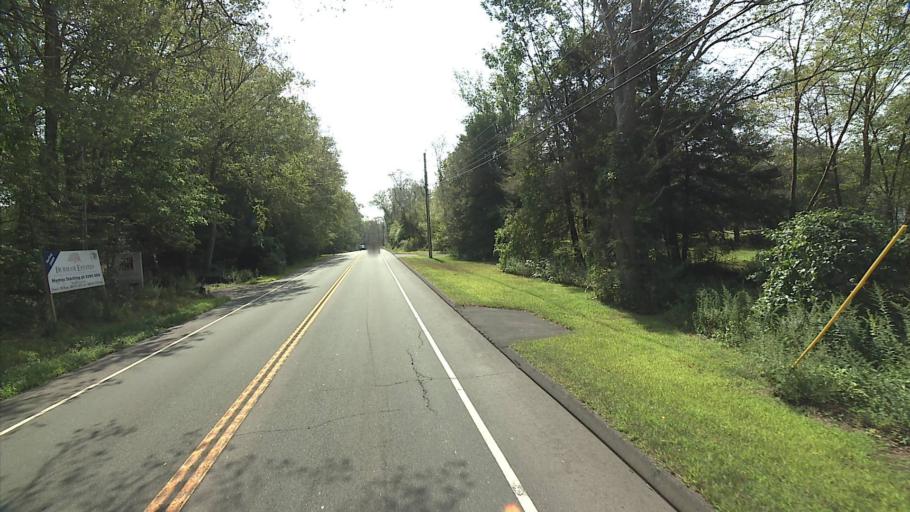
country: US
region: Connecticut
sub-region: Middlesex County
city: Durham
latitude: 41.4468
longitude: -72.6637
